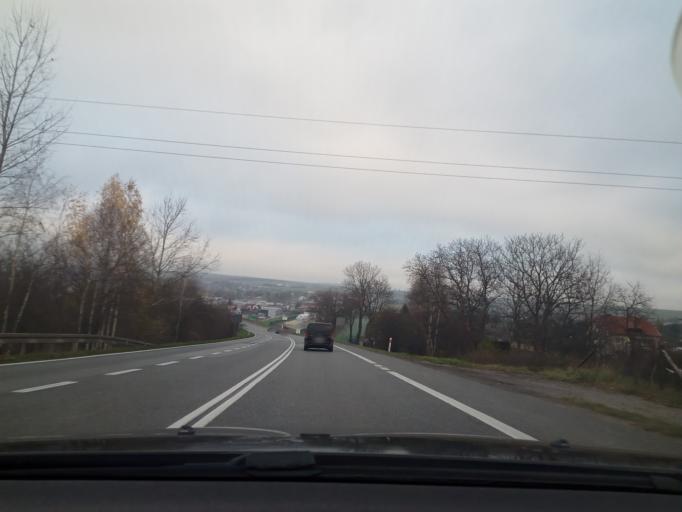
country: PL
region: Lesser Poland Voivodeship
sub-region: Powiat miechowski
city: Miechow
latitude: 50.3514
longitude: 20.0426
